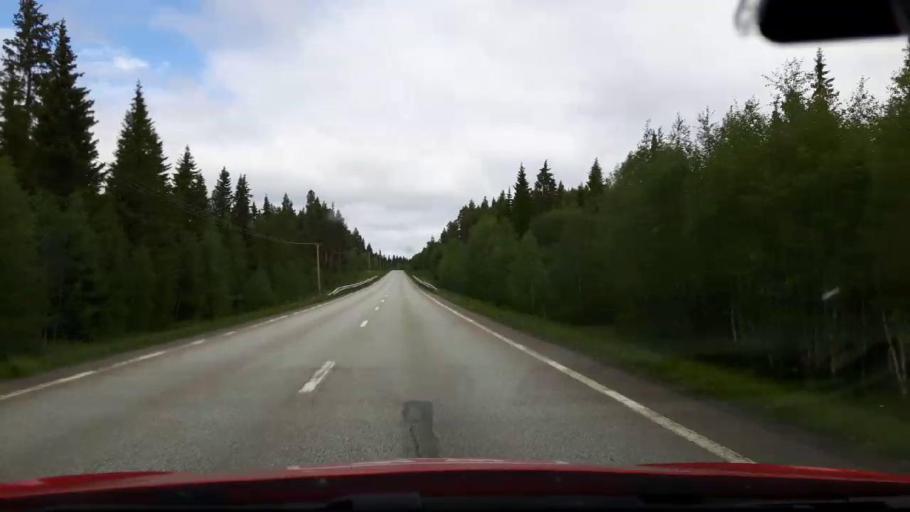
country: SE
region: Jaemtland
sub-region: Krokoms Kommun
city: Krokom
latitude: 63.4622
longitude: 14.4930
